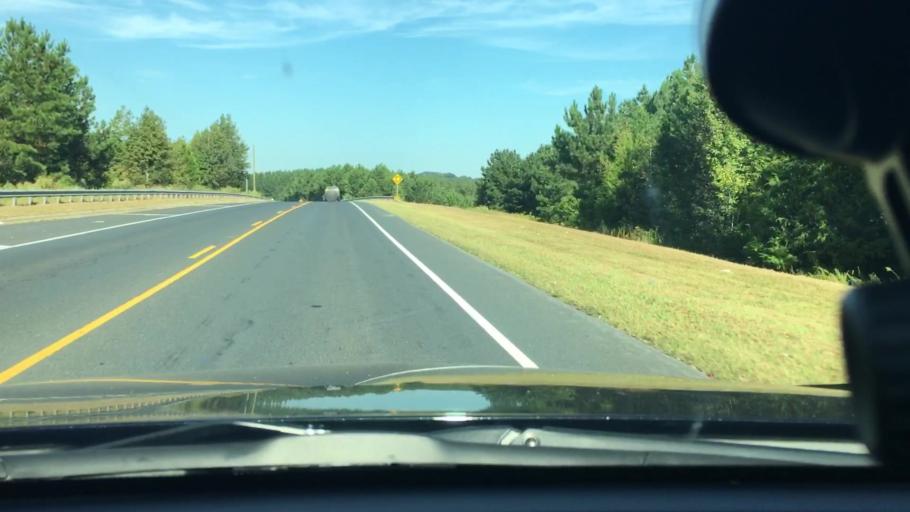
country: US
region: North Carolina
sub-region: Stanly County
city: Albemarle
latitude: 35.3837
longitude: -80.1796
